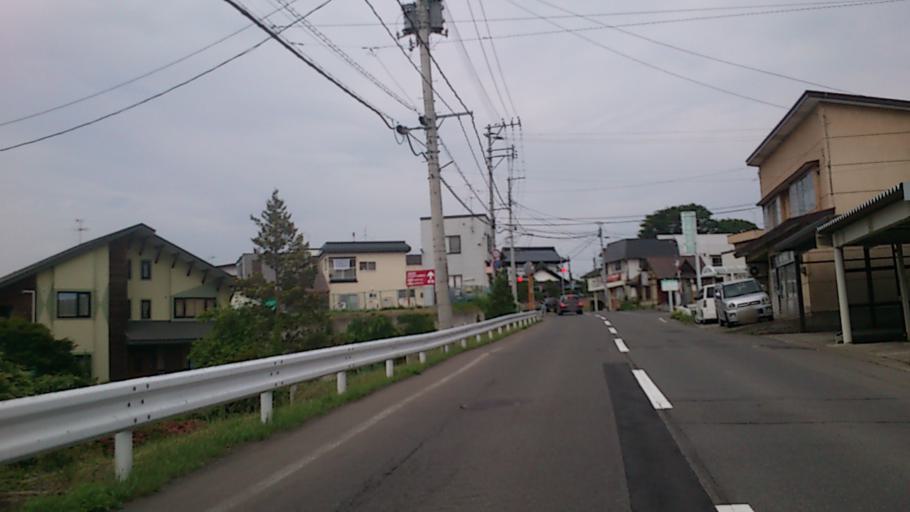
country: JP
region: Aomori
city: Hirosaki
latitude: 40.5946
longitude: 140.4536
